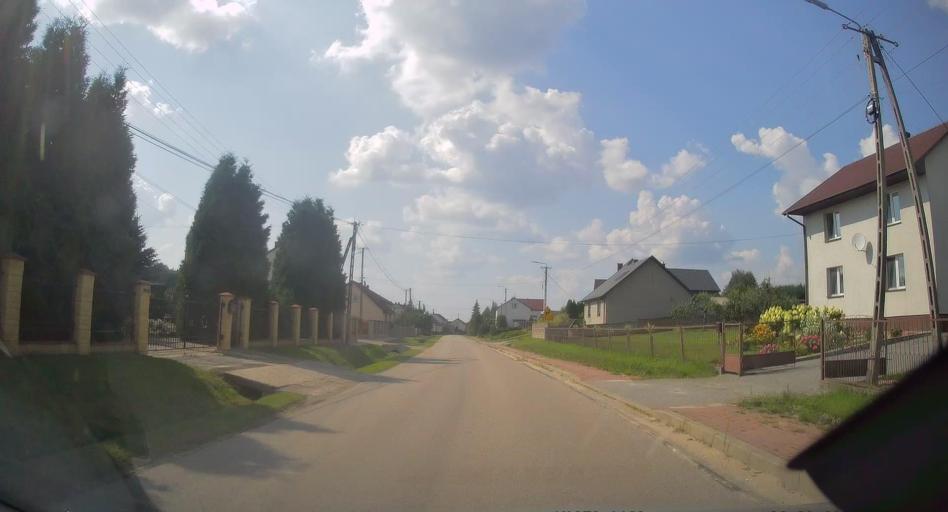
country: PL
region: Swietokrzyskie
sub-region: Powiat kielecki
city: Checiny
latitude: 50.8155
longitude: 20.4043
